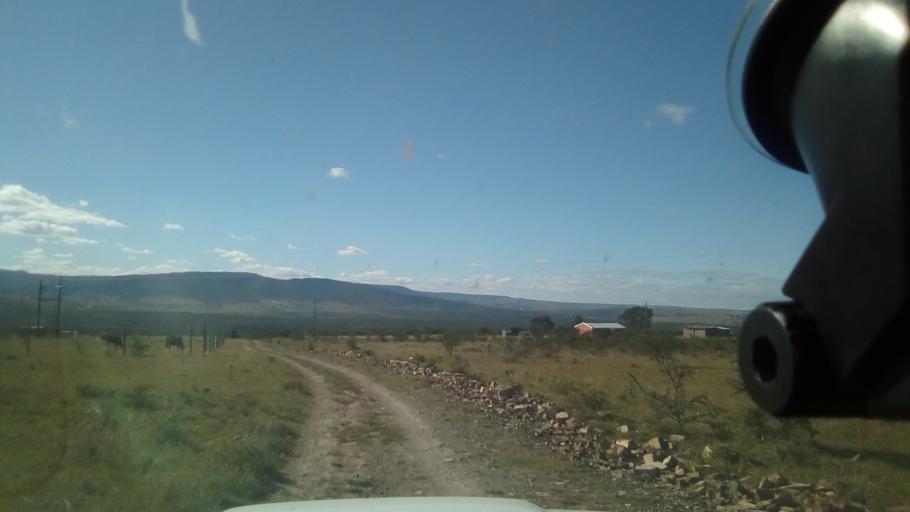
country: ZA
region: Eastern Cape
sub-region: Buffalo City Metropolitan Municipality
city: Bhisho
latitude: -32.7799
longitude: 27.3353
